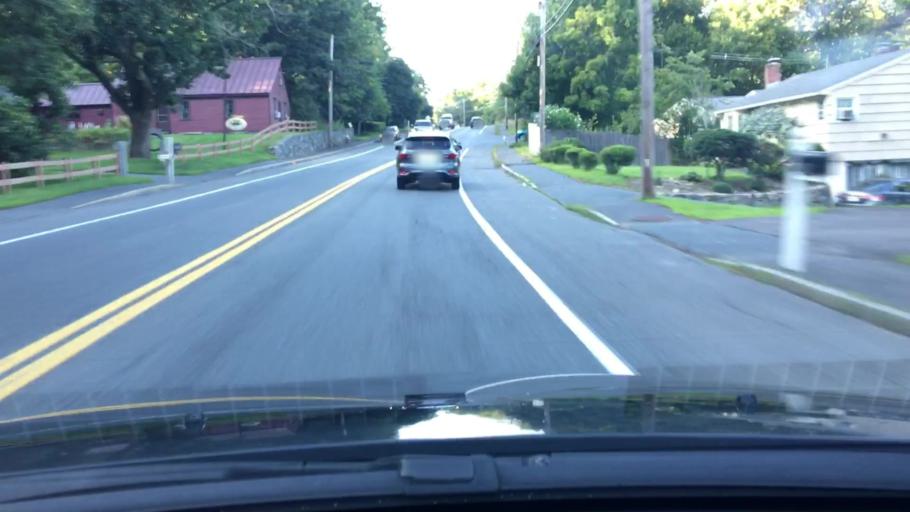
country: US
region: Massachusetts
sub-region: Worcester County
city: Shrewsbury
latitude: 42.3129
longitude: -71.7179
